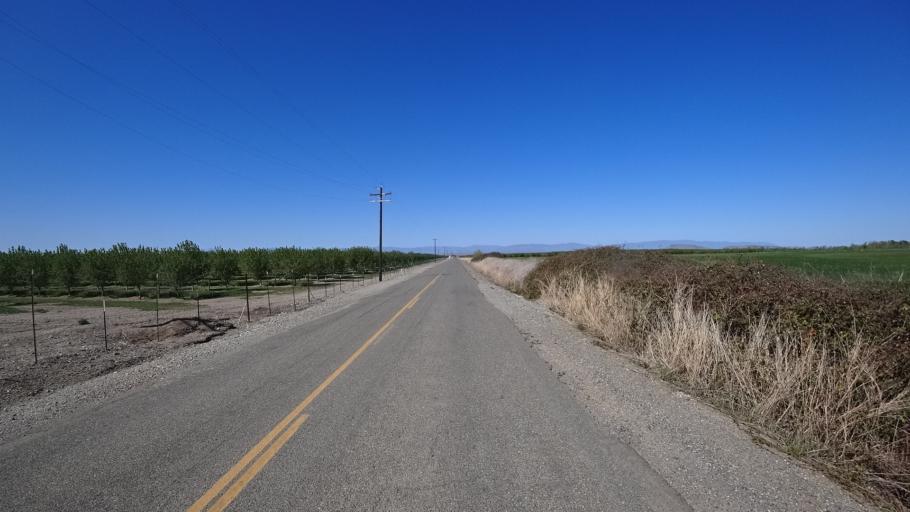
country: US
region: California
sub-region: Glenn County
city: Orland
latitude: 39.6972
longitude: -122.2290
